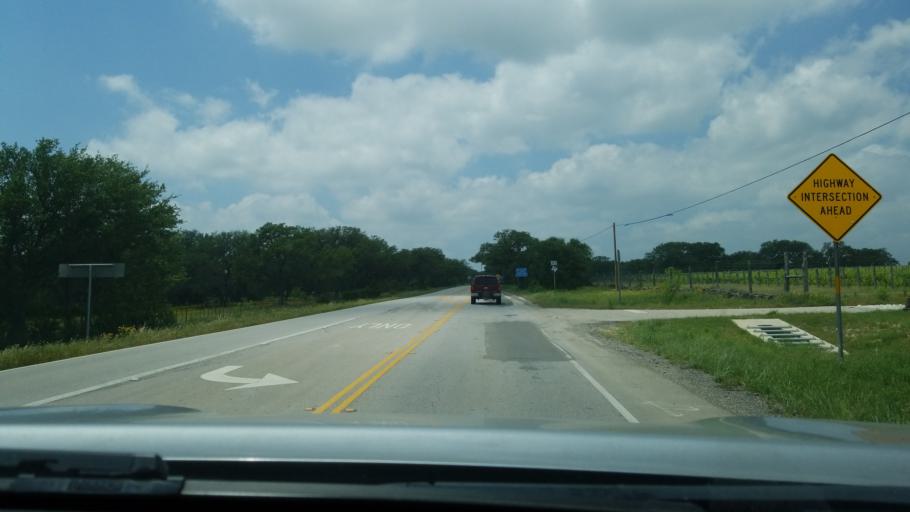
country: US
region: Texas
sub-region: Hays County
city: Dripping Springs
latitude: 30.1317
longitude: -98.0265
